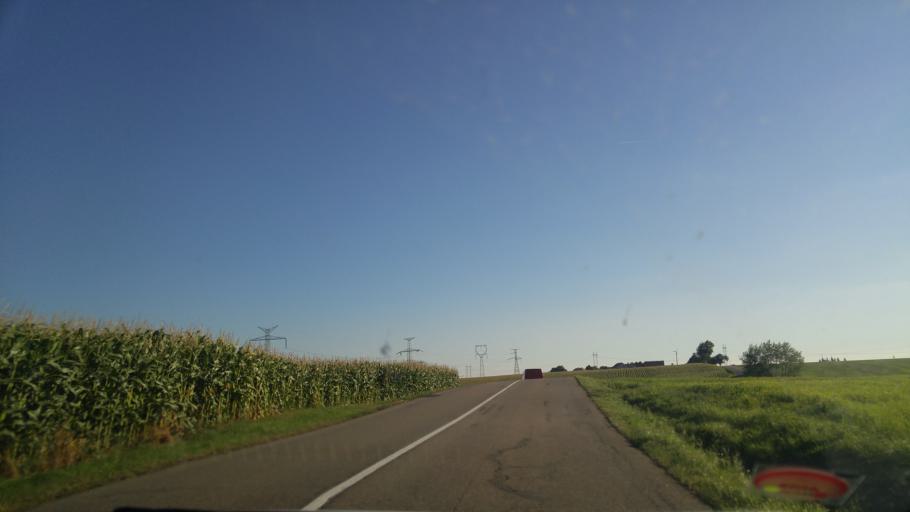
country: CZ
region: South Moravian
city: Ricany
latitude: 49.2238
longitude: 16.4164
